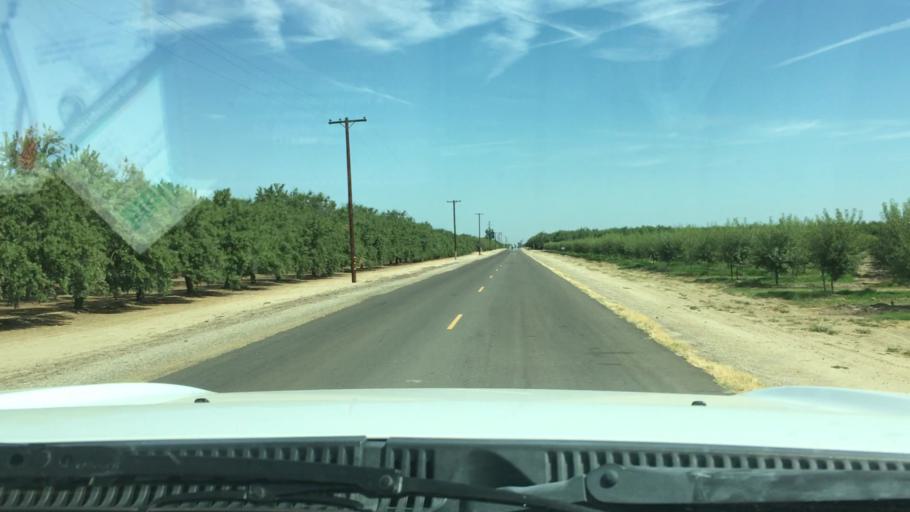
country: US
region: California
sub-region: Kern County
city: Wasco
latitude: 35.5225
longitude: -119.3499
